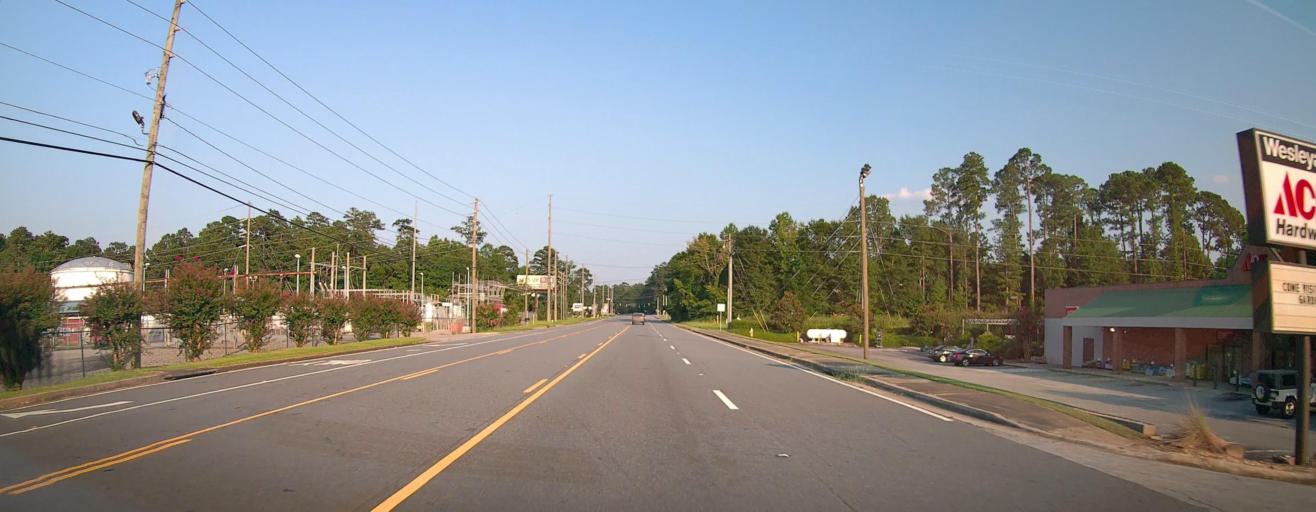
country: US
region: Georgia
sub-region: Bibb County
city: Macon
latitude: 32.8824
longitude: -83.7284
